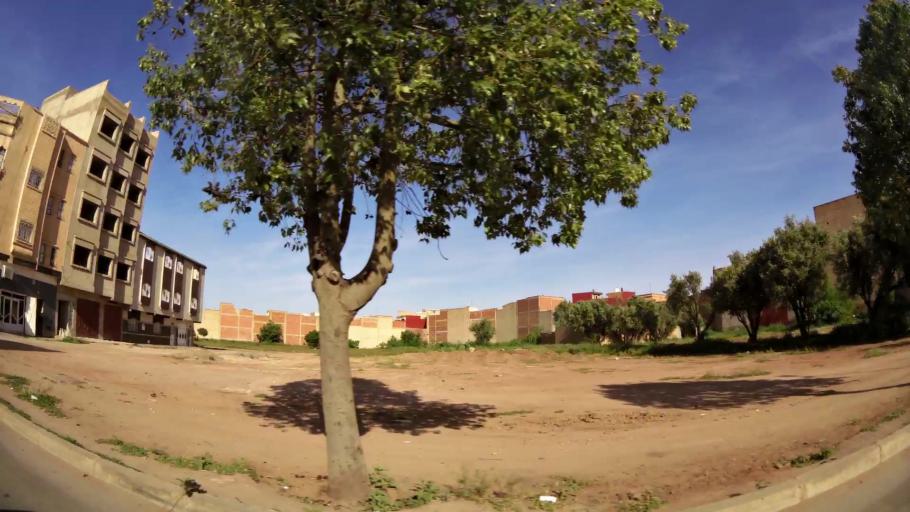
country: MA
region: Oriental
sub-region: Oujda-Angad
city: Oujda
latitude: 34.6675
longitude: -1.8958
